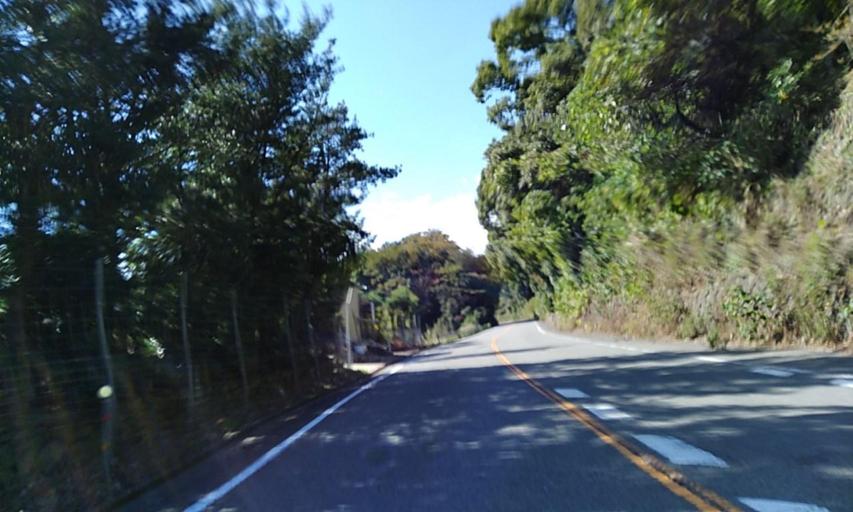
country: JP
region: Wakayama
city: Gobo
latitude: 33.9950
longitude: 135.1920
